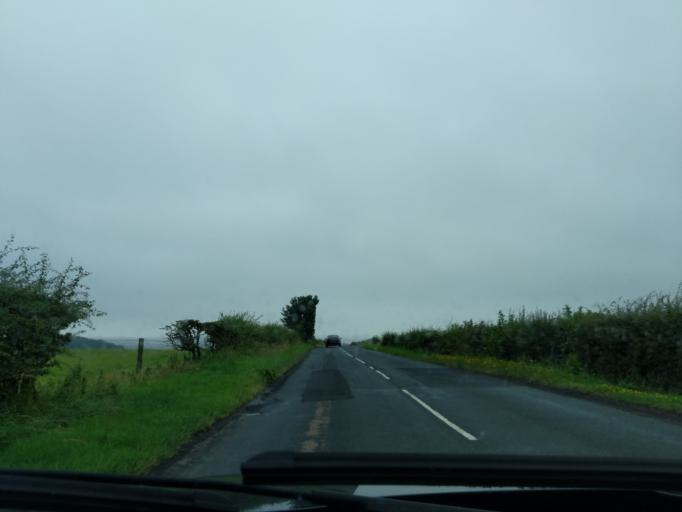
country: GB
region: England
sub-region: Northumberland
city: Lowick
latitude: 55.6578
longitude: -1.9219
